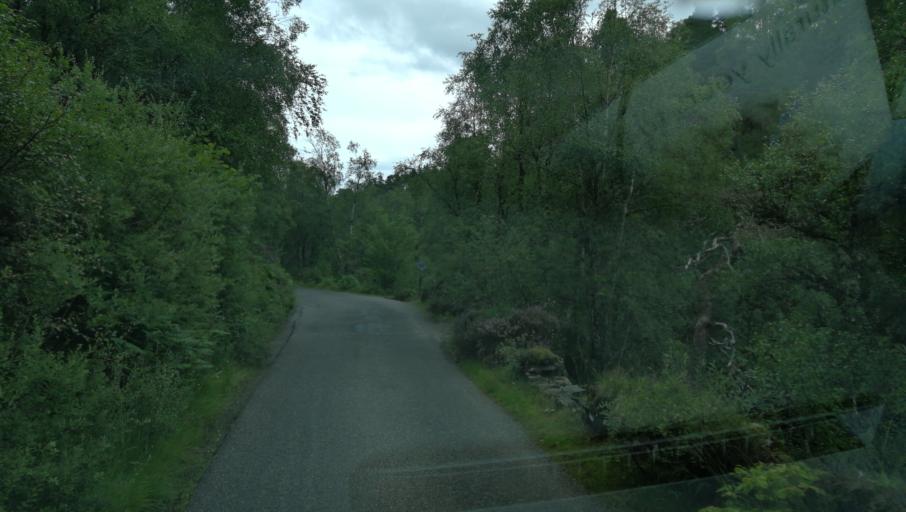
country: GB
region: Scotland
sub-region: Highland
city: Beauly
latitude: 57.3134
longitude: -4.8446
